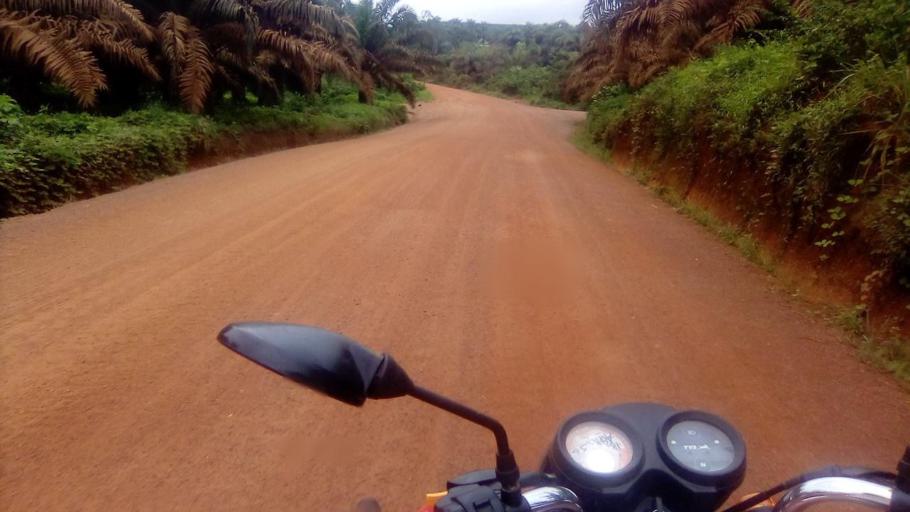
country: SL
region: Southern Province
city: Tongole
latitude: 7.4368
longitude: -11.8617
